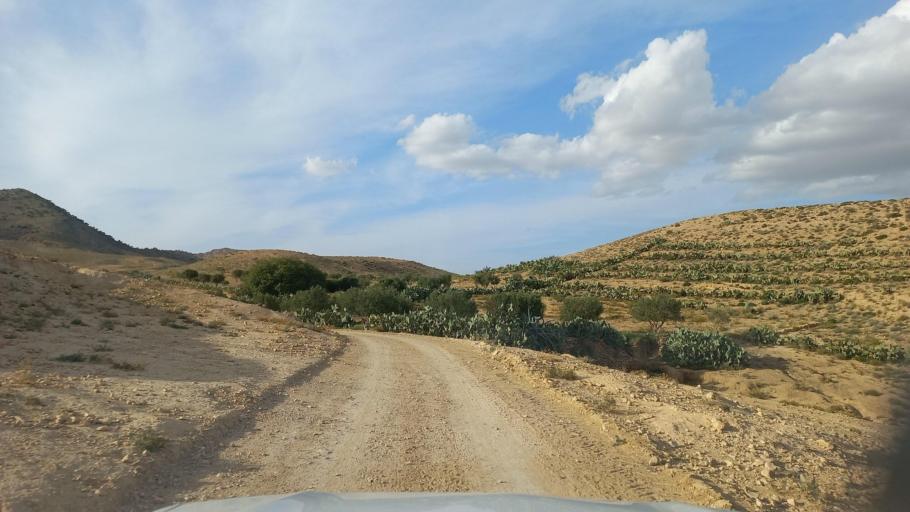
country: TN
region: Al Qasrayn
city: Sbiba
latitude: 35.4570
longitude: 9.0829
